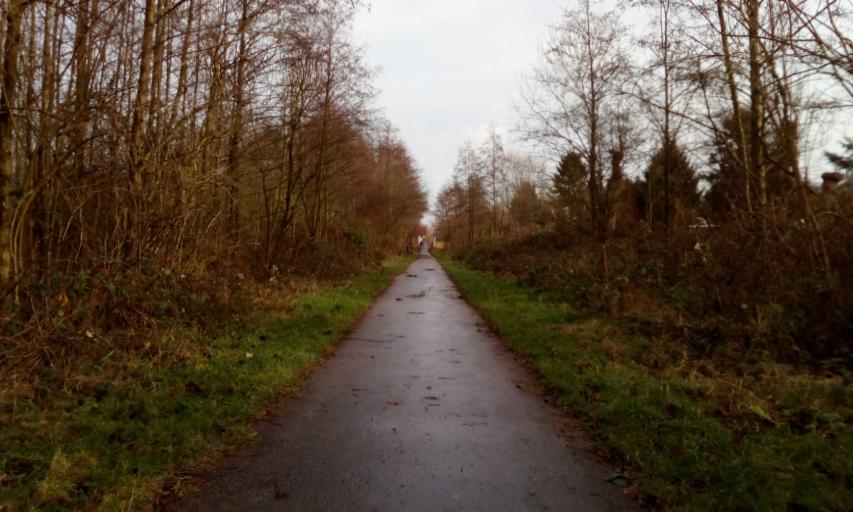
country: NL
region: South Holland
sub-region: Gemeente Lansingerland
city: Berkel en Rodenrijs
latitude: 51.9696
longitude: 4.4735
